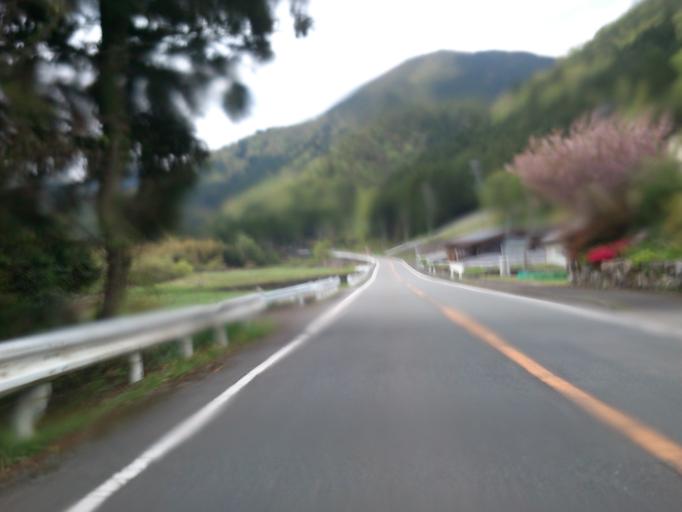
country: JP
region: Kyoto
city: Maizuru
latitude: 35.2789
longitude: 135.5415
